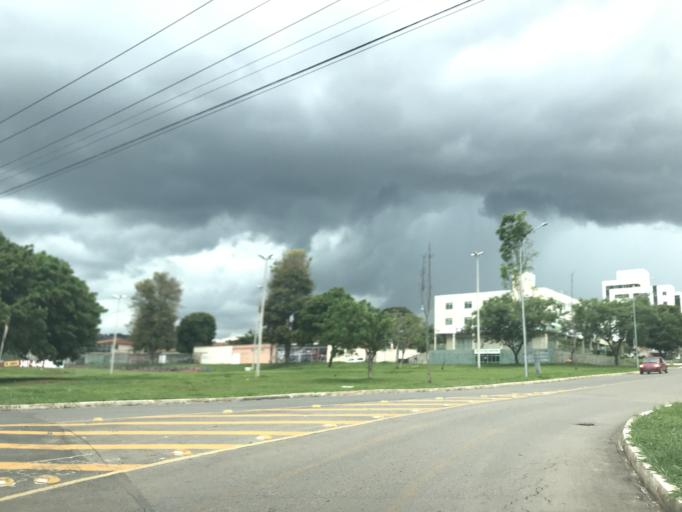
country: BR
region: Federal District
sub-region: Brasilia
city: Brasilia
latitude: -15.6461
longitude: -47.8114
